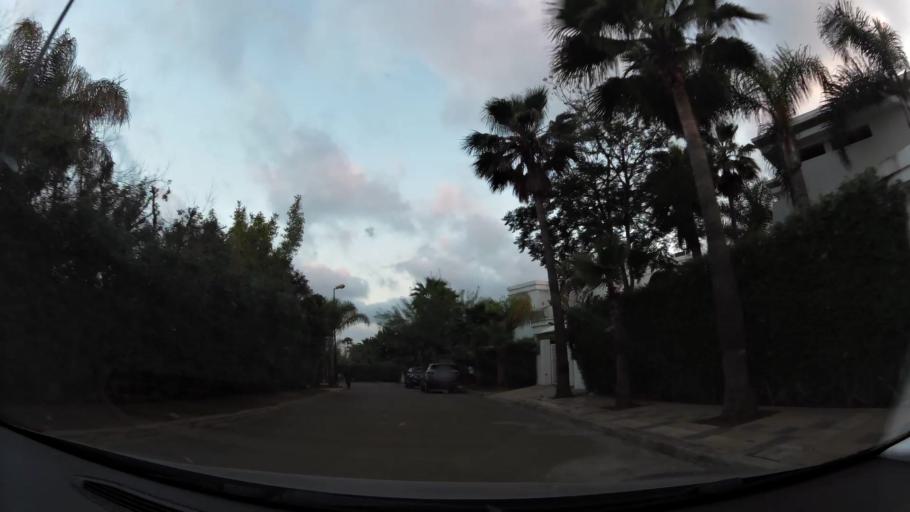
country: MA
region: Rabat-Sale-Zemmour-Zaer
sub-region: Rabat
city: Rabat
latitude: 33.9691
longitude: -6.8365
